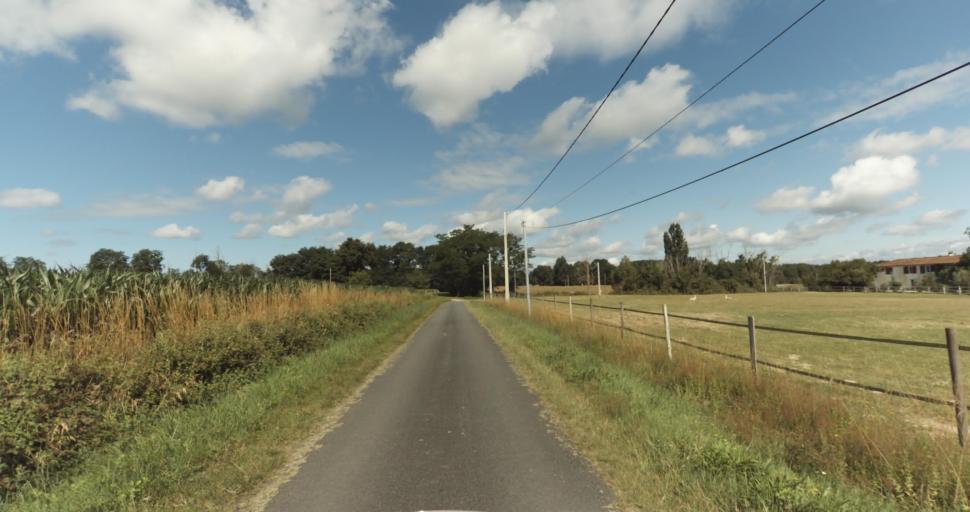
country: FR
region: Aquitaine
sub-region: Departement de la Gironde
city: Bazas
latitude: 44.4451
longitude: -0.1975
